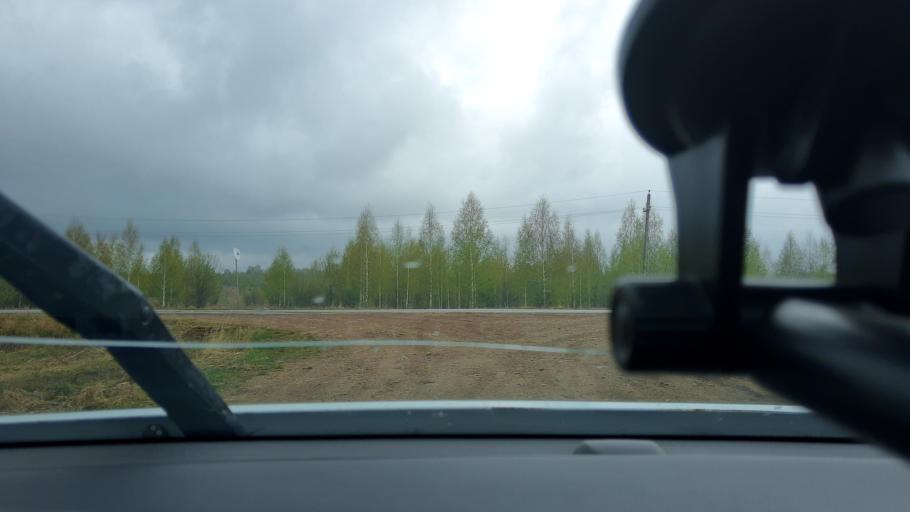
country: RU
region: Bashkortostan
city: Pavlovka
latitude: 55.4369
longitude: 56.3612
